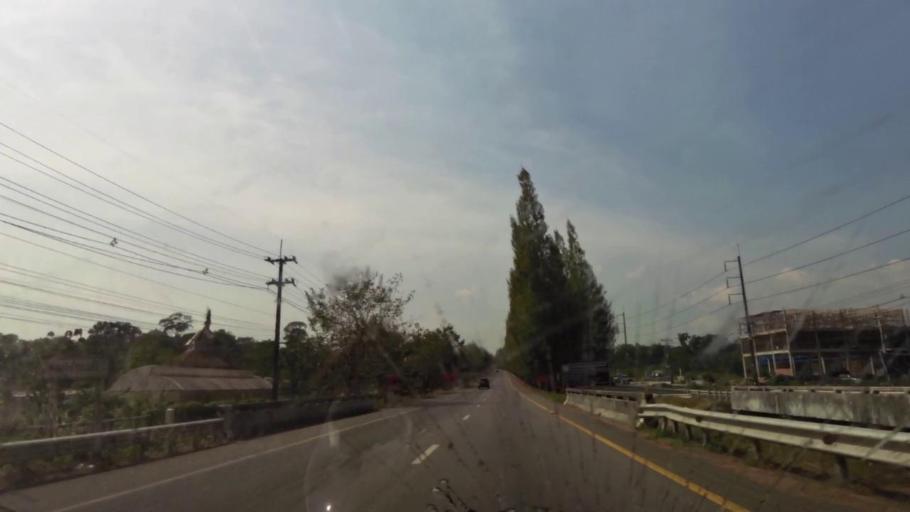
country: TH
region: Chanthaburi
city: Chanthaburi
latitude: 12.6660
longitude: 102.1010
